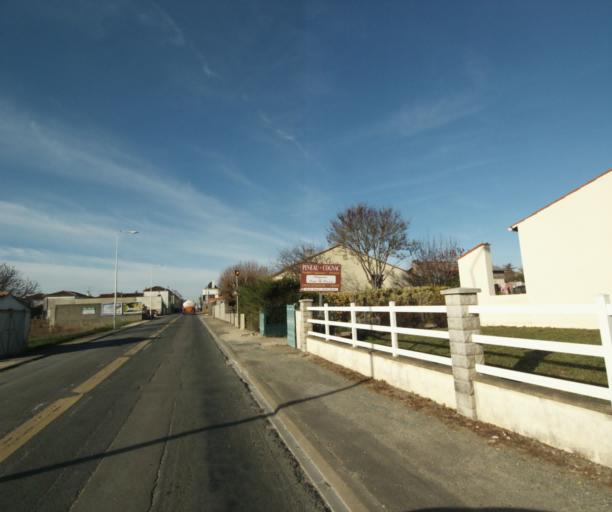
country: FR
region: Poitou-Charentes
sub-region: Departement de la Charente-Maritime
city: Burie
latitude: 45.7745
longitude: -0.4170
